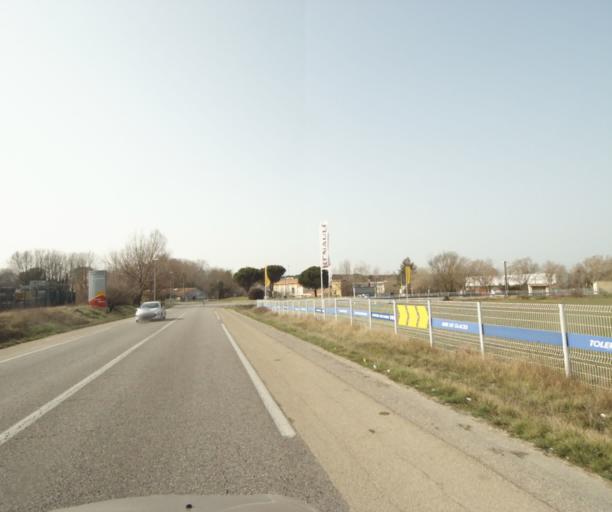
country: FR
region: Provence-Alpes-Cote d'Azur
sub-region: Departement des Bouches-du-Rhone
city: Cabries
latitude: 43.4257
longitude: 5.3890
